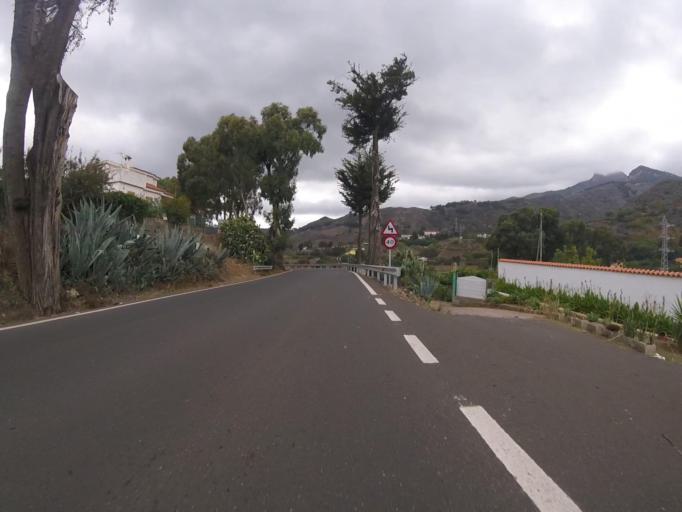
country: ES
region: Canary Islands
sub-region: Provincia de Las Palmas
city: Vega de San Mateo
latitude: 28.0088
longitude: -15.5429
